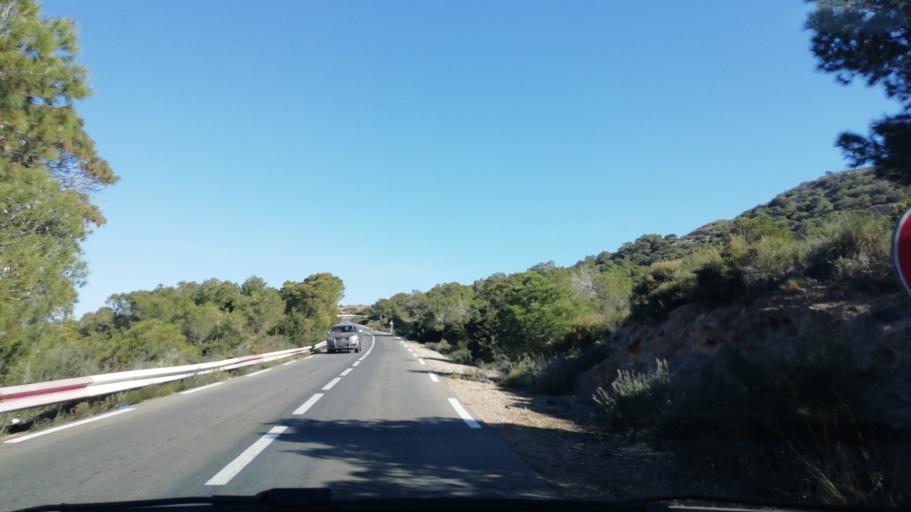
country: DZ
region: Ain Temouchent
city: El Amria
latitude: 35.6434
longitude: -1.0519
